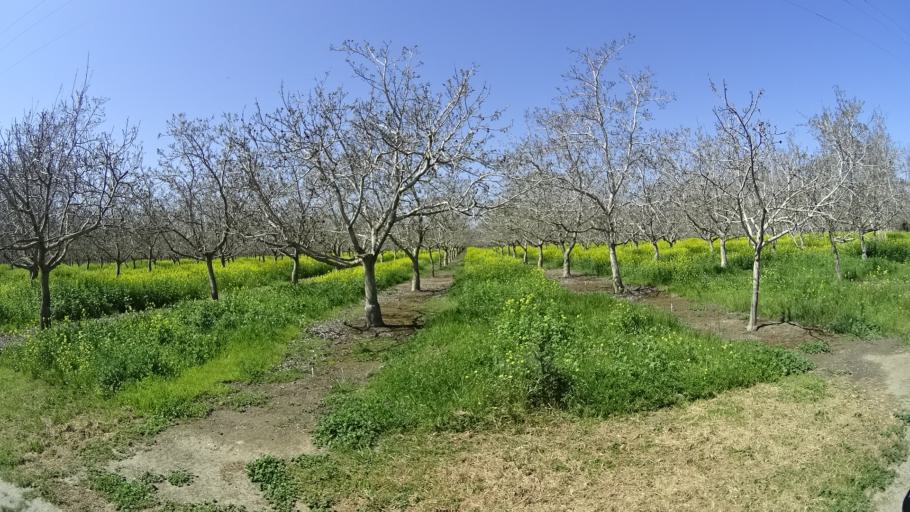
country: US
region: California
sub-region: Glenn County
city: Willows
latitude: 39.4404
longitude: -121.9863
